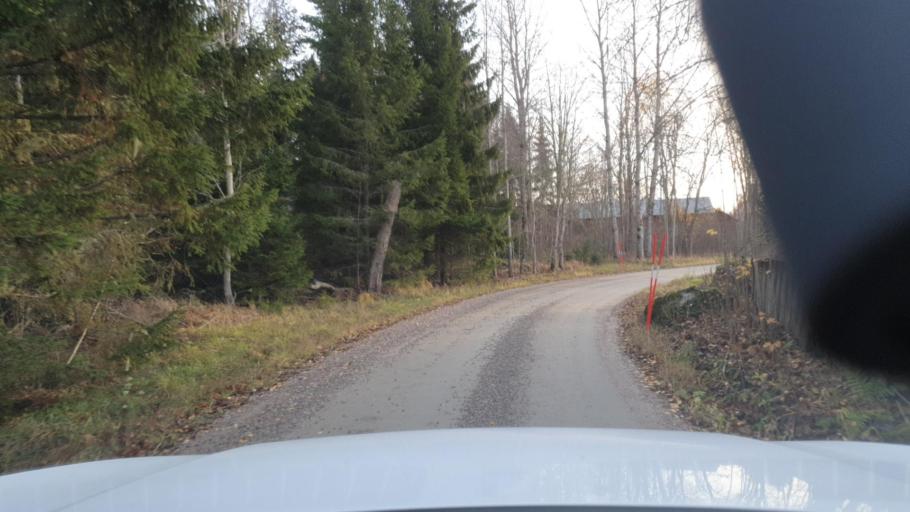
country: SE
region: Uppsala
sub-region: Alvkarleby Kommun
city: AElvkarleby
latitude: 60.4840
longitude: 17.5132
